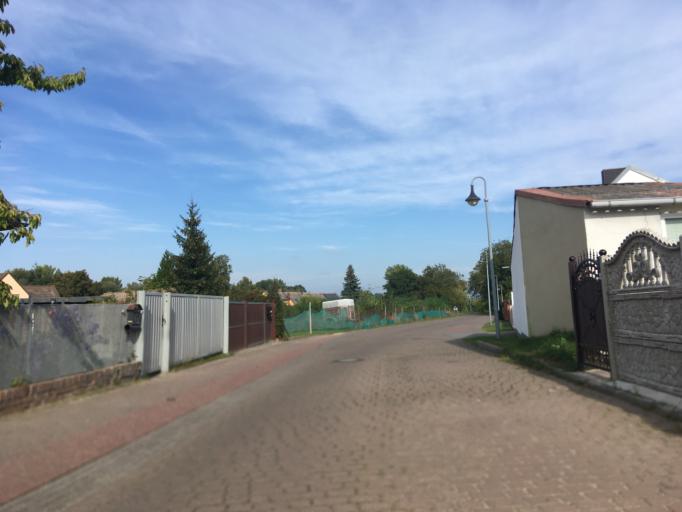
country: DE
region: Brandenburg
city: Oderberg
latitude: 52.8447
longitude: 14.1221
